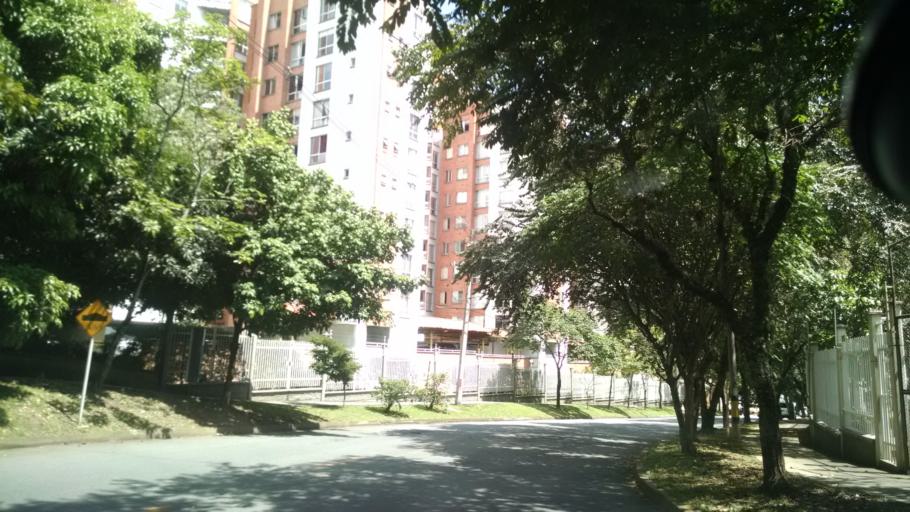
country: CO
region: Antioquia
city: Itagui
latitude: 6.2216
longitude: -75.6036
